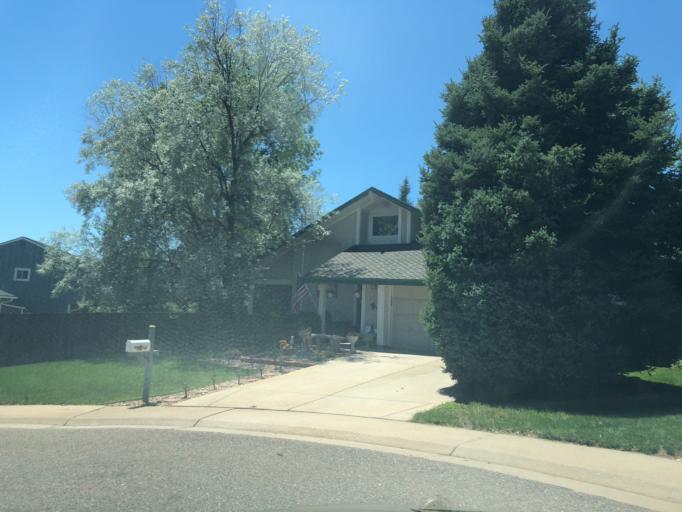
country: US
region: Colorado
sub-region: Arapahoe County
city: Dove Valley
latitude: 39.6164
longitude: -104.7755
